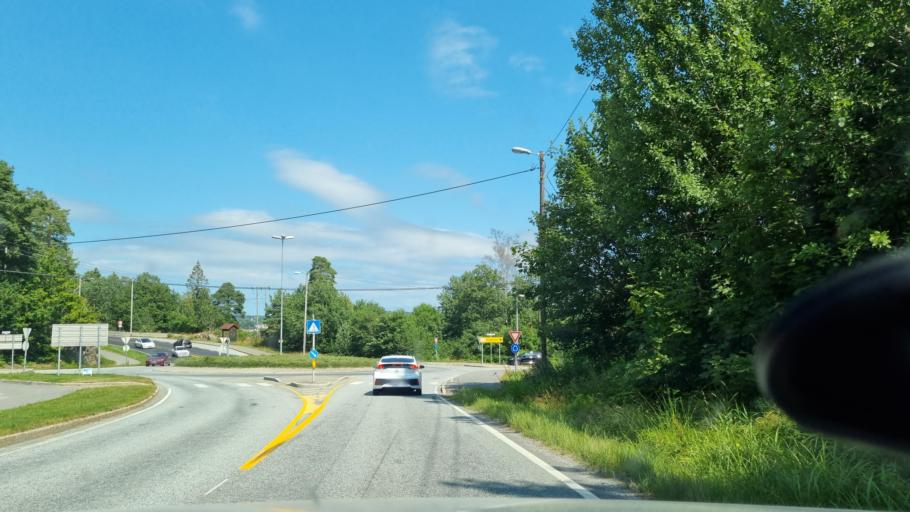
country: NO
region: Aust-Agder
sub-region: Arendal
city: Arendal
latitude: 58.4663
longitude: 8.8243
